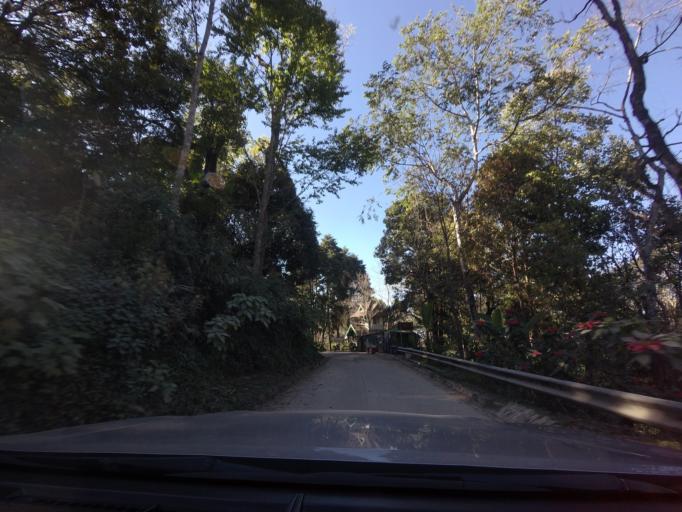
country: TH
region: Chiang Mai
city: Mae On
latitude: 18.8560
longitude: 99.3675
